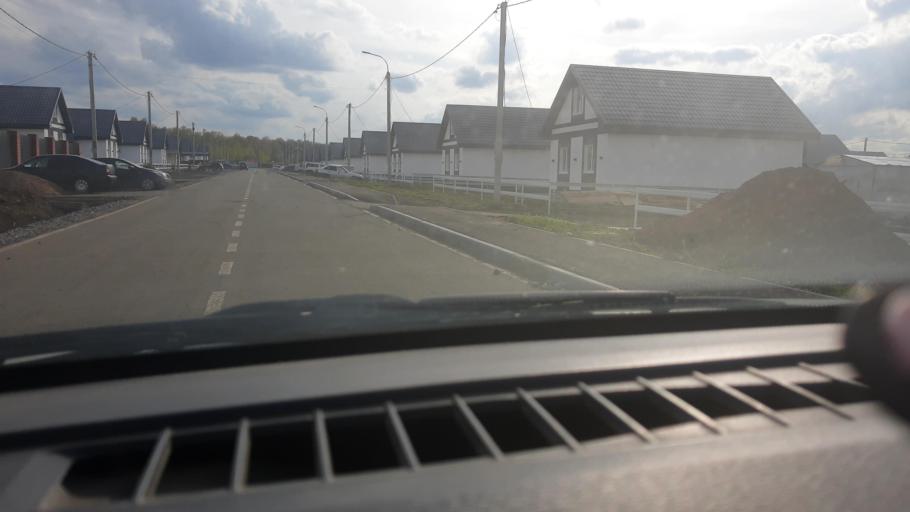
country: RU
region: Bashkortostan
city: Avdon
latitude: 54.4825
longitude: 55.8931
